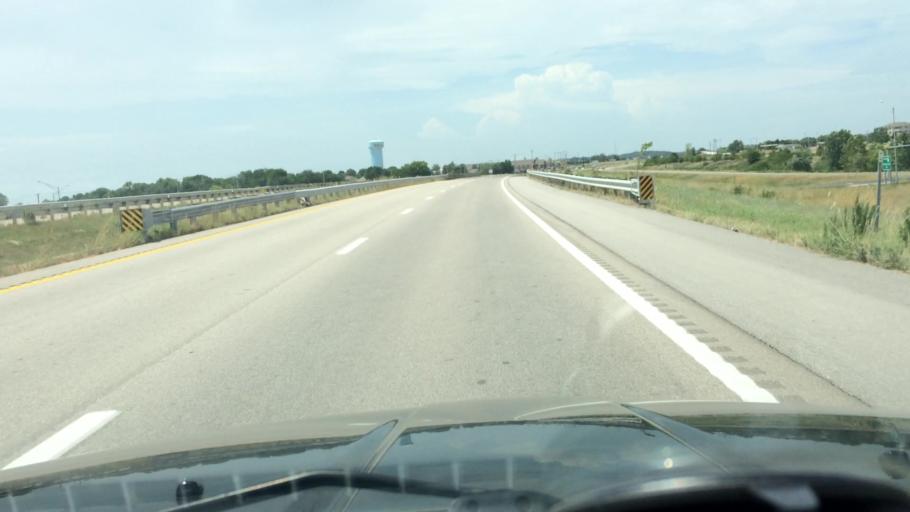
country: US
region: Missouri
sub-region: Polk County
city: Bolivar
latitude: 37.5920
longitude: -93.4309
